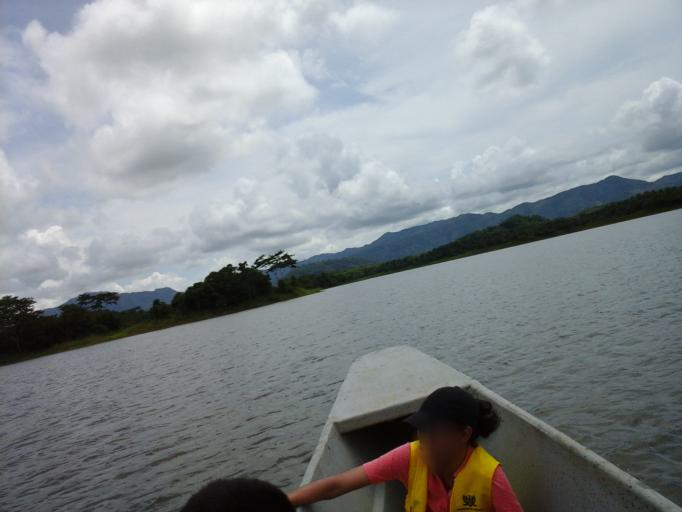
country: CO
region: Bolivar
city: San Cristobal
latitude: 9.8721
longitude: -75.2949
